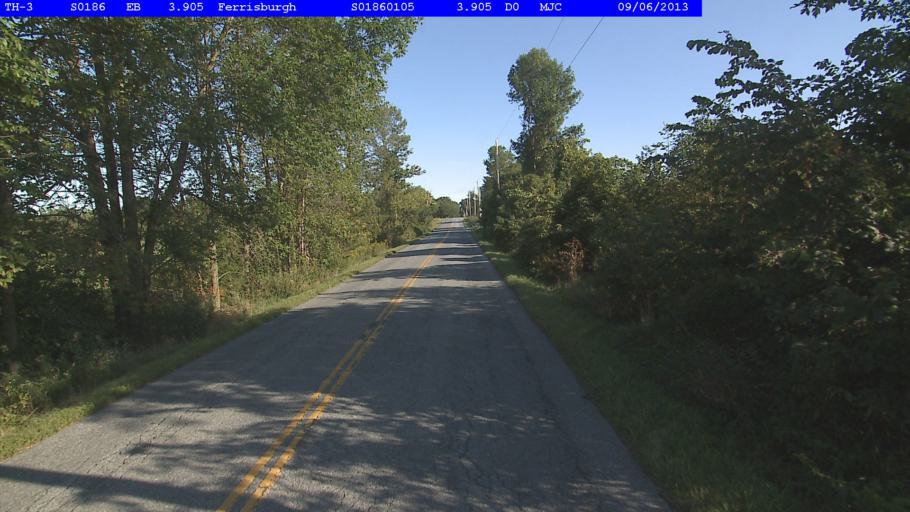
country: US
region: Vermont
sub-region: Addison County
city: Vergennes
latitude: 44.1717
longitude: -73.3025
